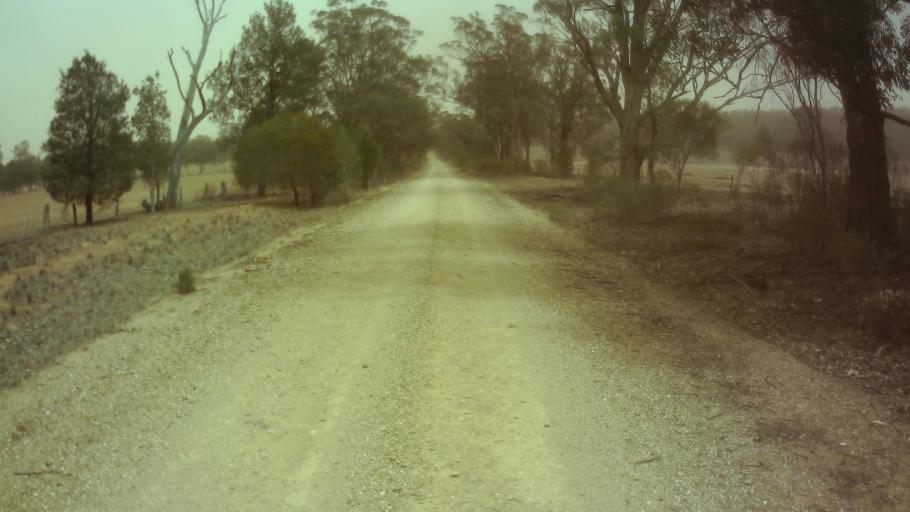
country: AU
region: New South Wales
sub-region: Weddin
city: Grenfell
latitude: -33.7104
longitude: 147.9557
